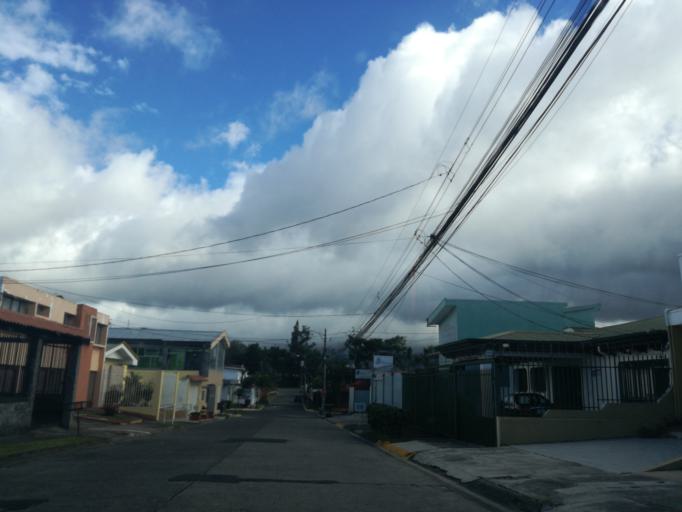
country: CR
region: San Jose
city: San Pedro
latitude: 9.9260
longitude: -84.0423
